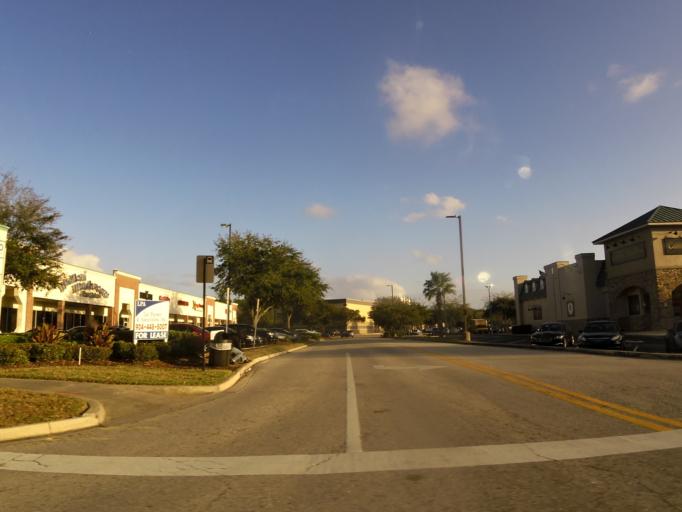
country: US
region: Florida
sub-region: Duval County
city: Jacksonville
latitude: 30.2651
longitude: -81.5557
